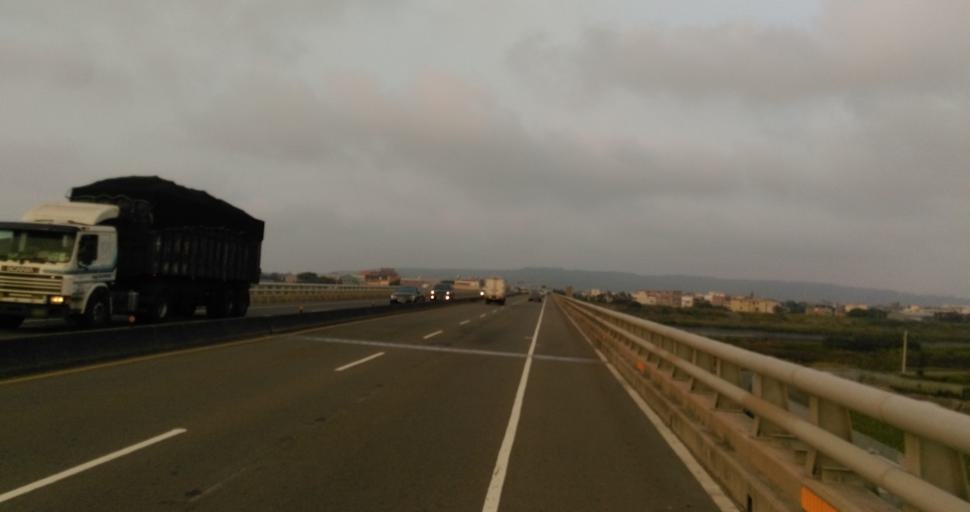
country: TW
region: Taiwan
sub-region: Hsinchu
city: Hsinchu
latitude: 24.8476
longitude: 120.9389
